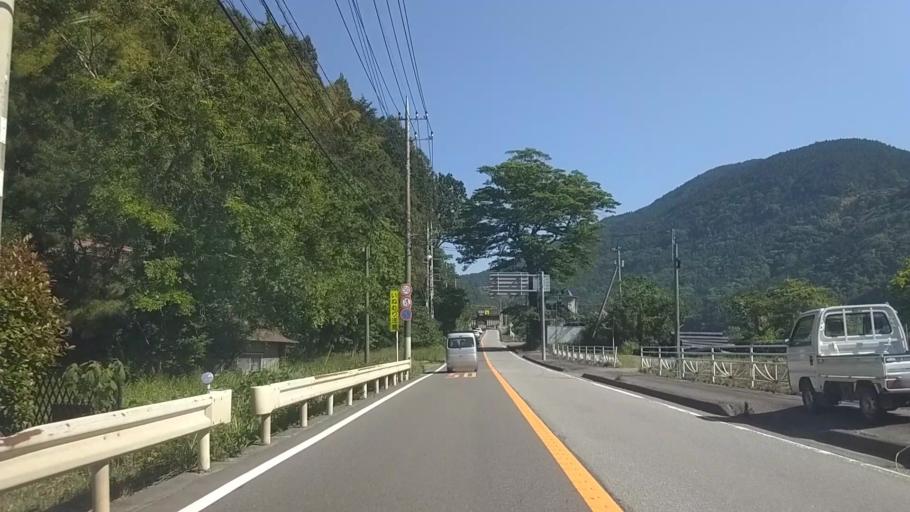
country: JP
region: Shizuoka
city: Fujinomiya
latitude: 35.2530
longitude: 138.4786
